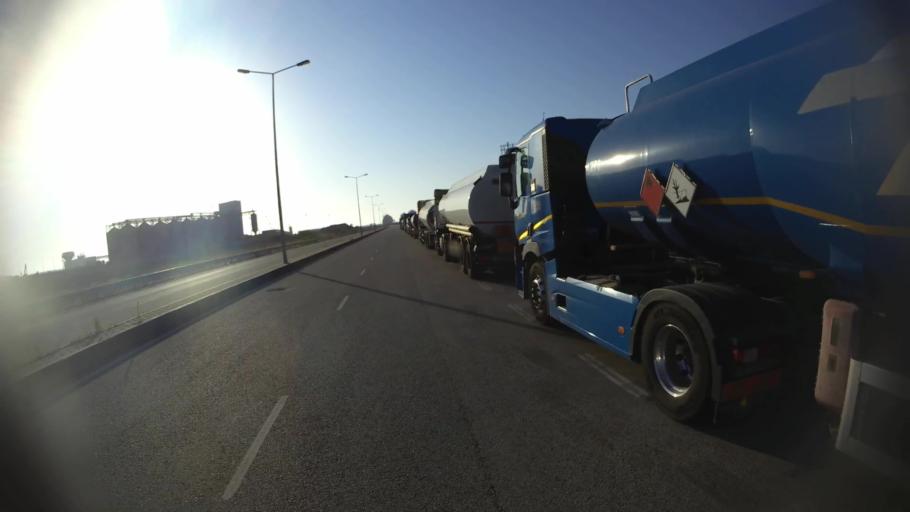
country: PT
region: Aveiro
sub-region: Ilhavo
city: Gafanha da Nazare
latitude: 40.6520
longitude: -8.7065
